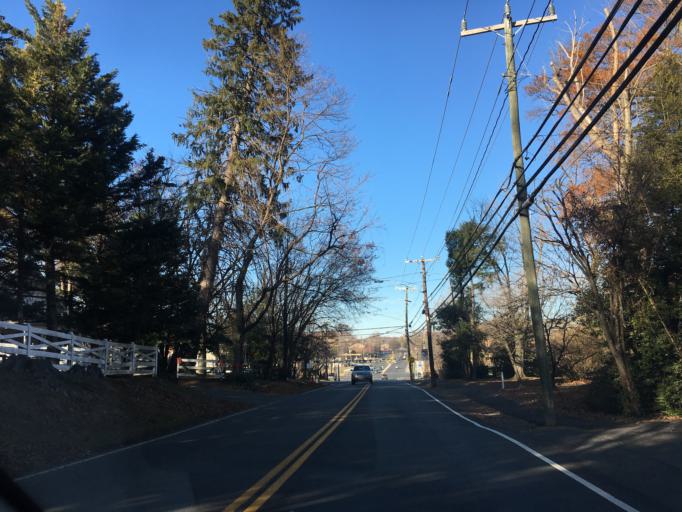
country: US
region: Virginia
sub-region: City of Fairfax
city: Fairfax
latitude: 38.8558
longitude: -77.3074
